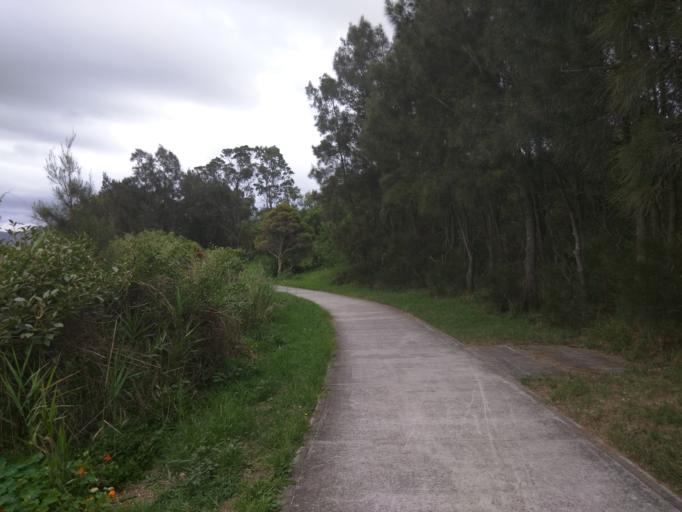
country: AU
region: New South Wales
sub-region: Wollongong
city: Berkeley
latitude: -34.4857
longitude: 150.8589
